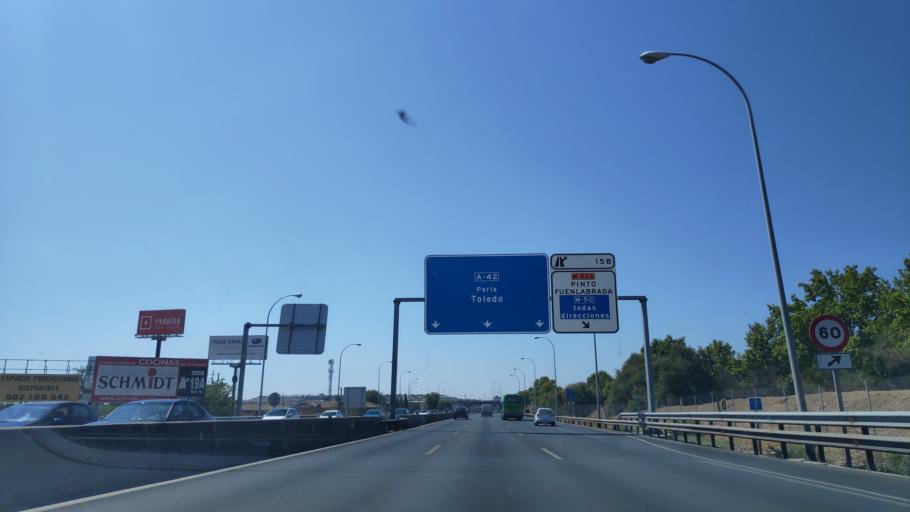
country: ES
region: Madrid
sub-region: Provincia de Madrid
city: Getafe
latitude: 40.2849
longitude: -3.7447
